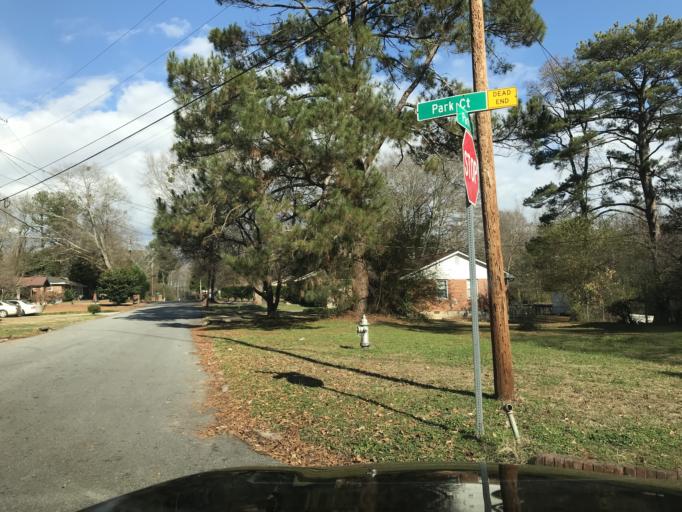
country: US
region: Georgia
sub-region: Clayton County
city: Morrow
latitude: 33.5881
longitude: -84.3731
